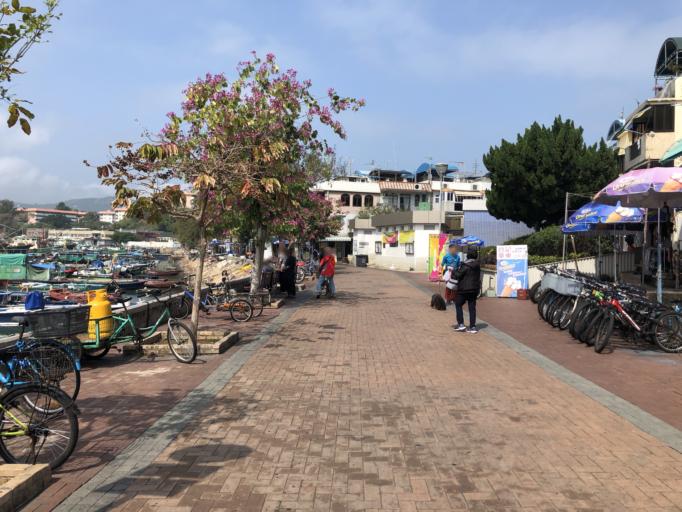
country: HK
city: Yung Shue Wan
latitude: 22.2102
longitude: 114.0284
